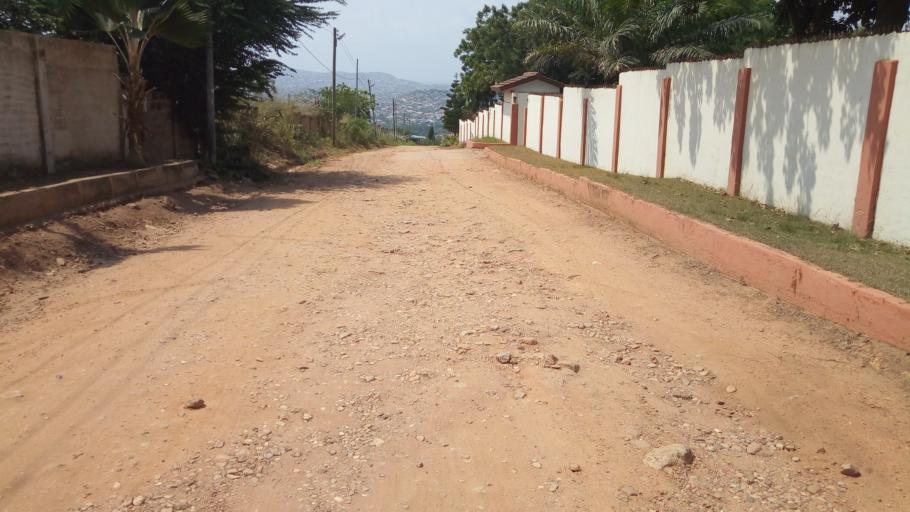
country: GH
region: Greater Accra
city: Gbawe
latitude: 5.5630
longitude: -0.3030
